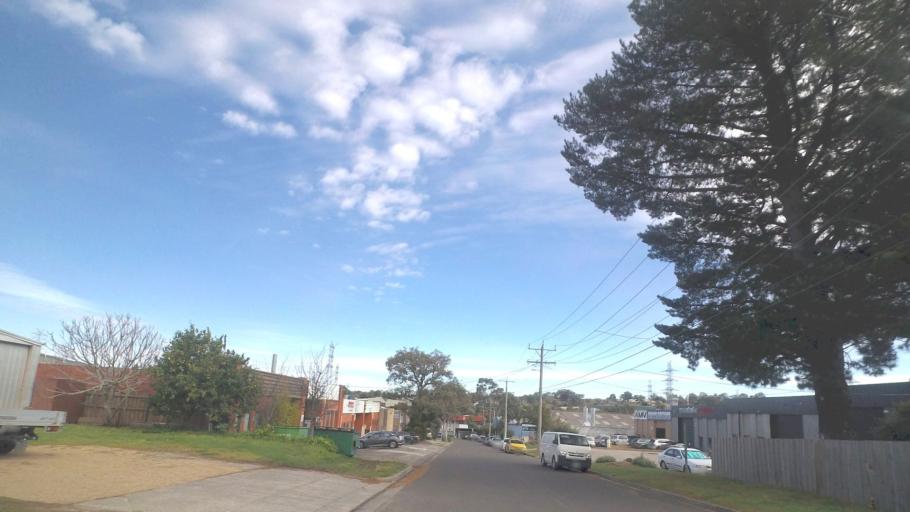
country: AU
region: Victoria
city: Mitcham
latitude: -37.8244
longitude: 145.2202
